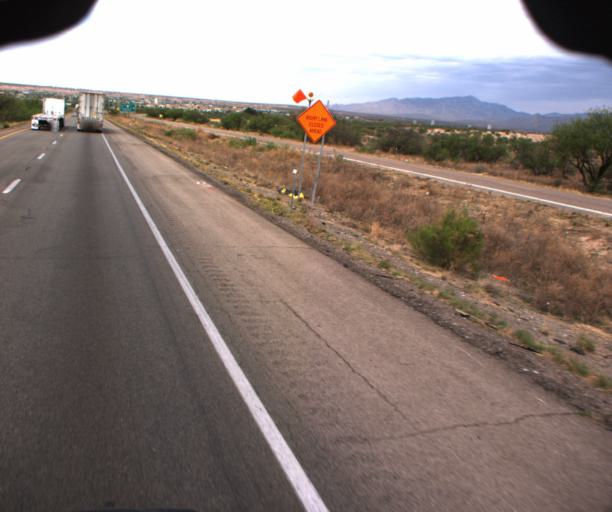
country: US
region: Arizona
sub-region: Cochise County
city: Benson
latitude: 31.9654
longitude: -110.2619
